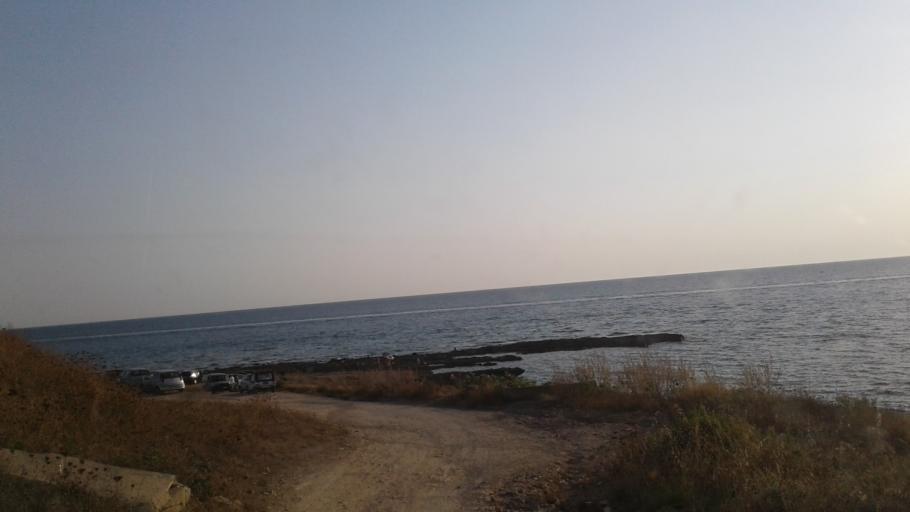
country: IT
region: Sardinia
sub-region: Provincia di Sassari
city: Alghero
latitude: 40.5449
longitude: 8.3215
